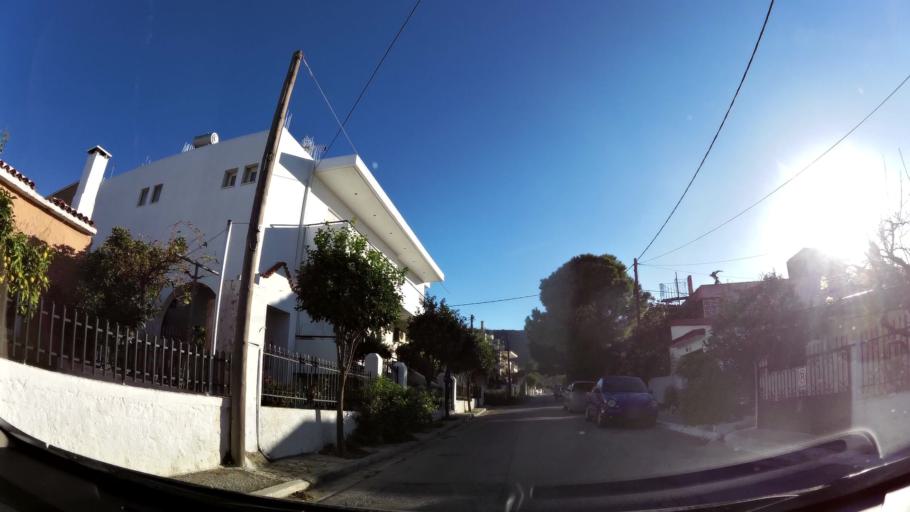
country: GR
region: Attica
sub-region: Nomarchia Anatolikis Attikis
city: Kalyvia Thorikou
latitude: 37.8350
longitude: 23.9284
